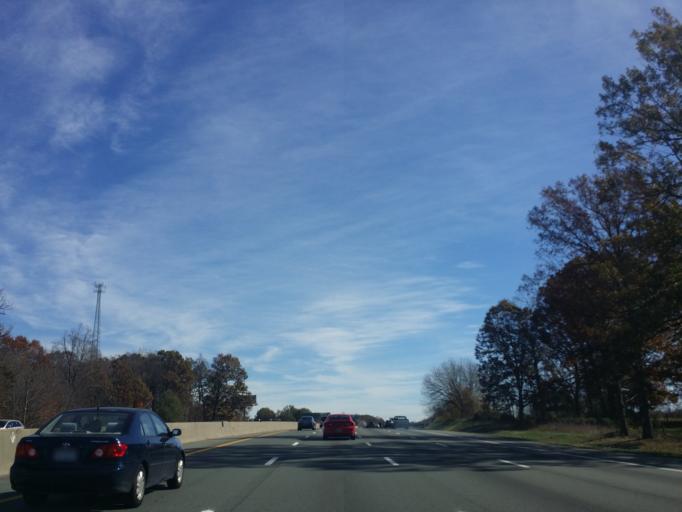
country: US
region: North Carolina
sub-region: Alamance County
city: Haw River
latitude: 36.0686
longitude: -79.3376
